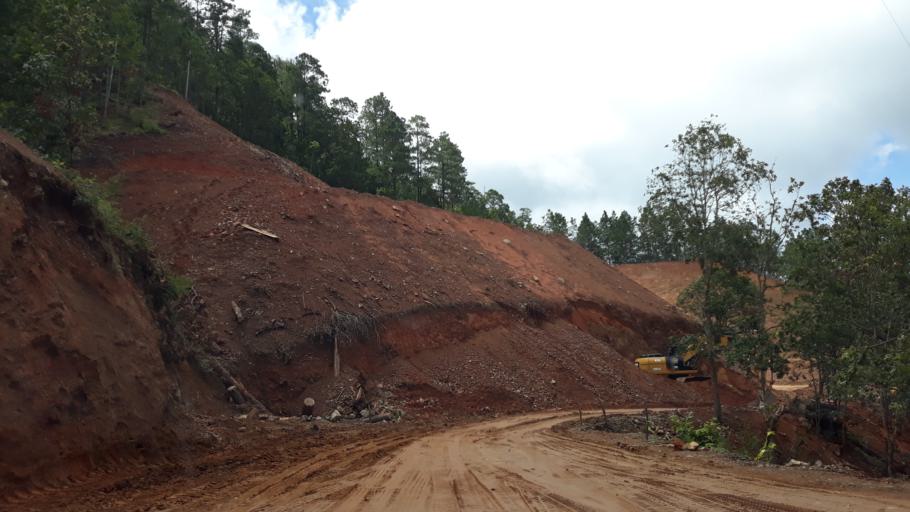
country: HN
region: El Paraiso
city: Santa Cruz
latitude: 13.7591
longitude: -86.6508
